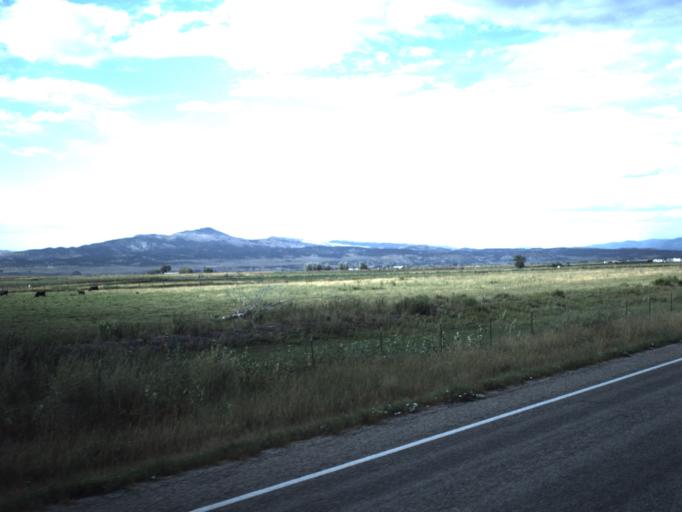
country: US
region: Utah
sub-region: Sanpete County
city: Mount Pleasant
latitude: 39.4952
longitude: -111.5094
